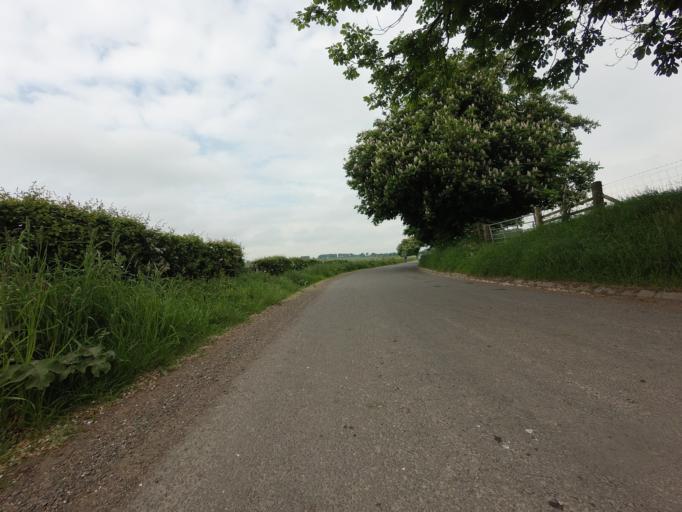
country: GB
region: Scotland
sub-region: Perth and Kinross
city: Kinross
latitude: 56.1713
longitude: -3.4457
